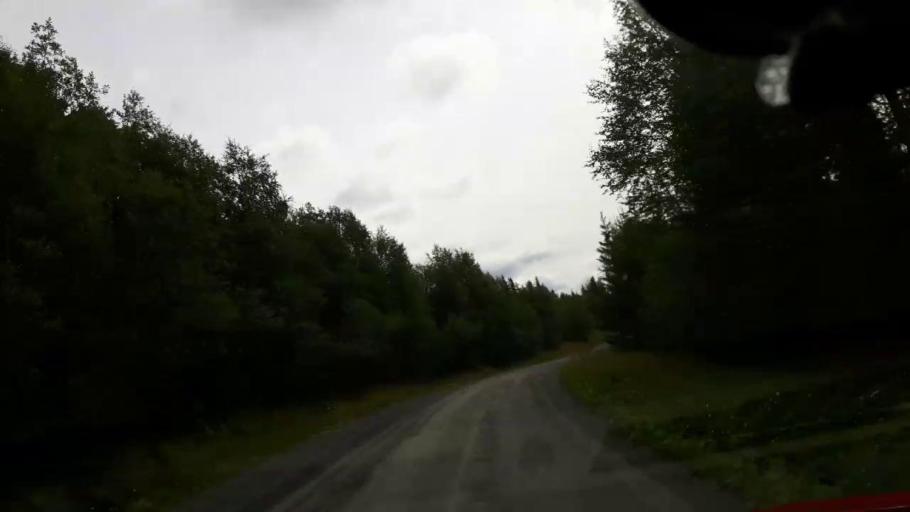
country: SE
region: Jaemtland
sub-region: Krokoms Kommun
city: Valla
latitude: 63.6659
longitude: 13.9653
